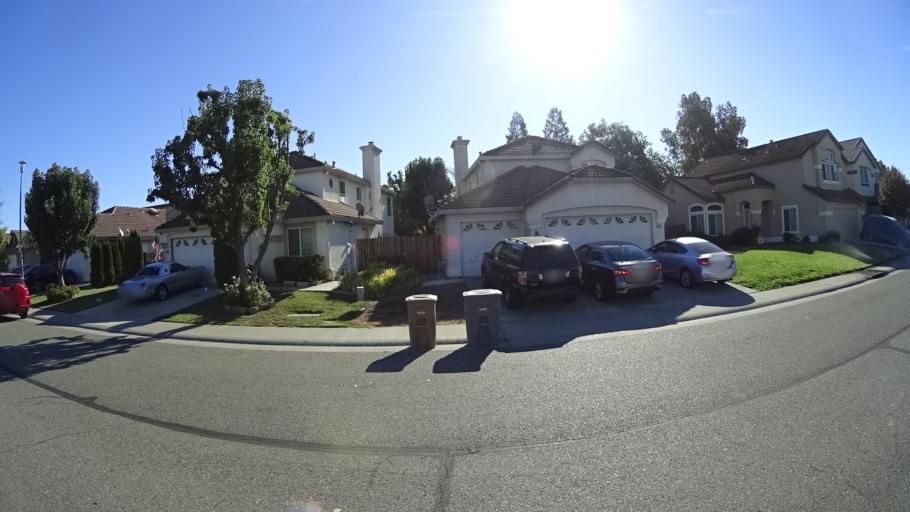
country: US
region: California
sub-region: Sacramento County
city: Elk Grove
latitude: 38.4409
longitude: -121.3873
